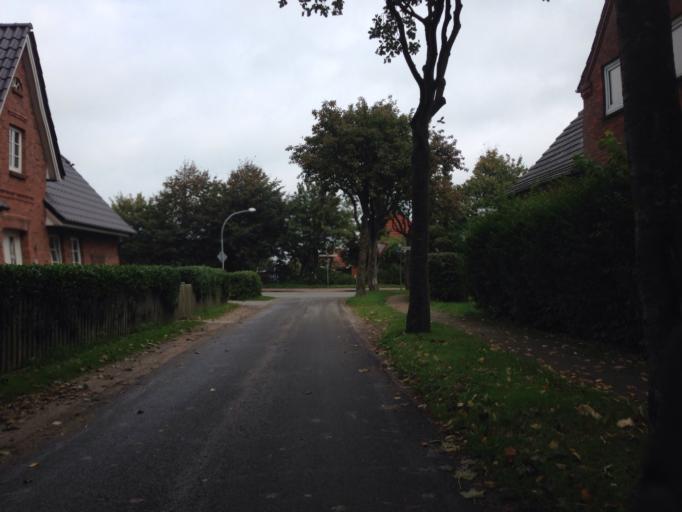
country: DE
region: Schleswig-Holstein
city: Wrixum
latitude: 54.6970
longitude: 8.5520
